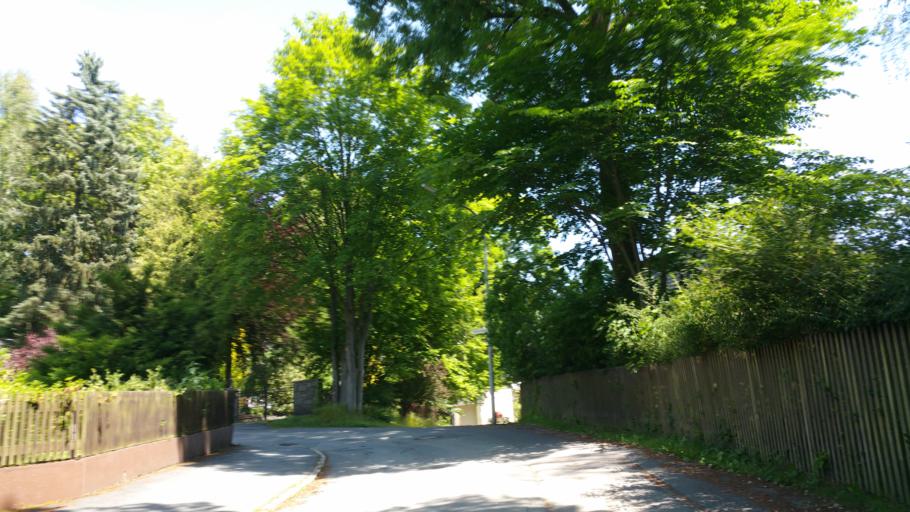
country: DE
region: Bavaria
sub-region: Upper Franconia
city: Schwarzenbach an der Saale
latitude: 50.2236
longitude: 11.9301
